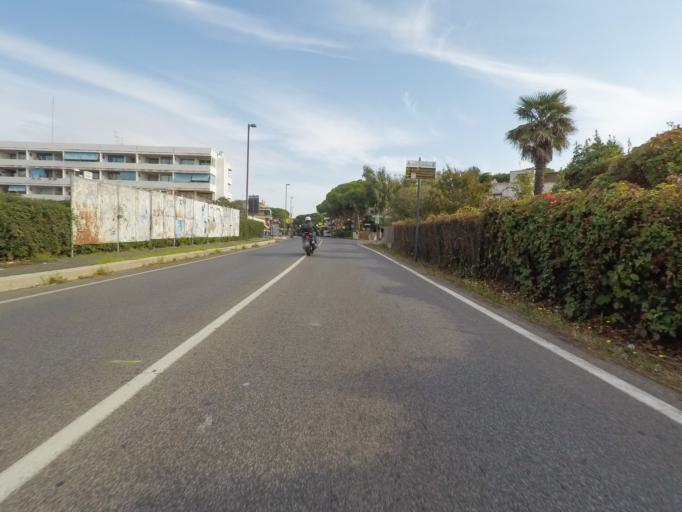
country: IT
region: Latium
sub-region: Citta metropolitana di Roma Capitale
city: Santa Marinella
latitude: 42.0336
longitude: 11.8364
